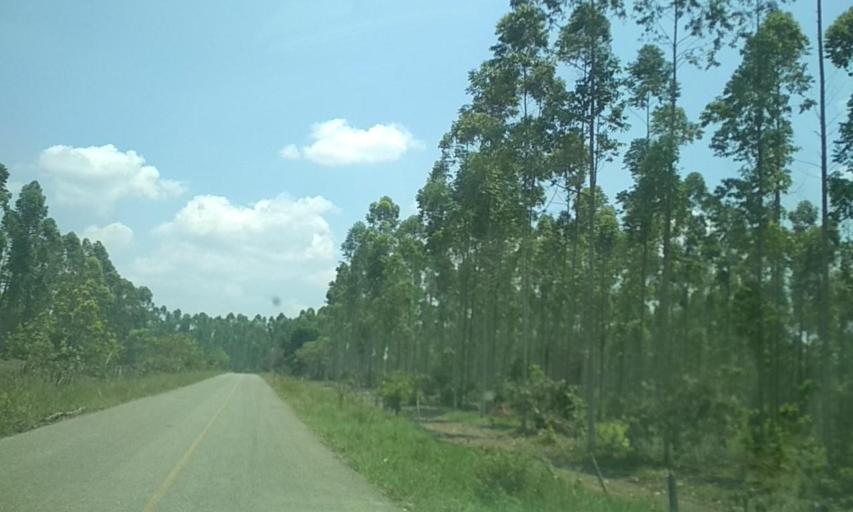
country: MX
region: Tabasco
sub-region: Huimanguillo
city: Francisco Rueda
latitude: 17.8368
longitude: -93.8828
